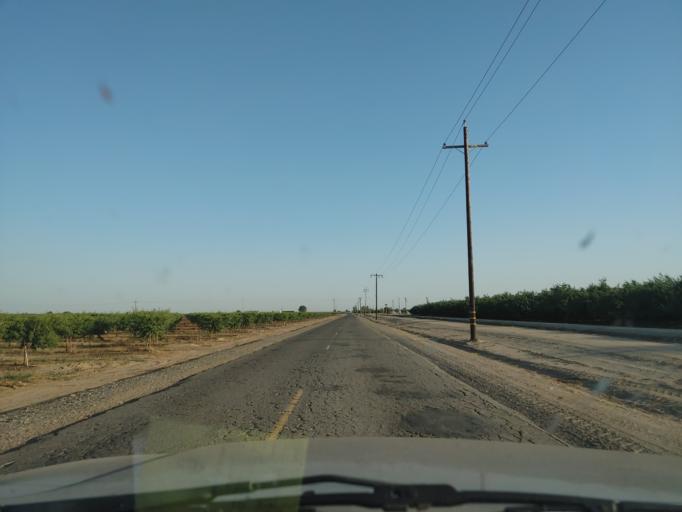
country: US
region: California
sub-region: Madera County
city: Chowchilla
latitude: 37.1303
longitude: -120.3829
